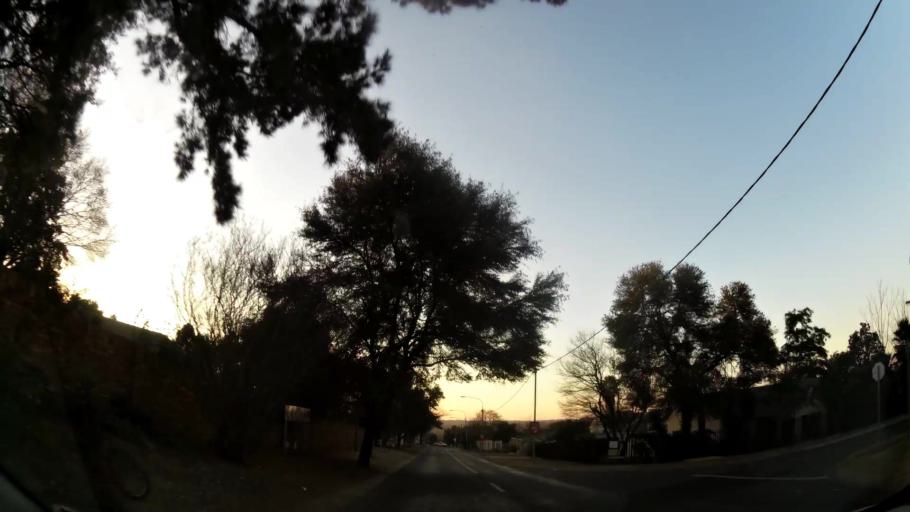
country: ZA
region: Gauteng
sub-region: City of Tshwane Metropolitan Municipality
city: Centurion
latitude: -25.8426
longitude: 28.1560
